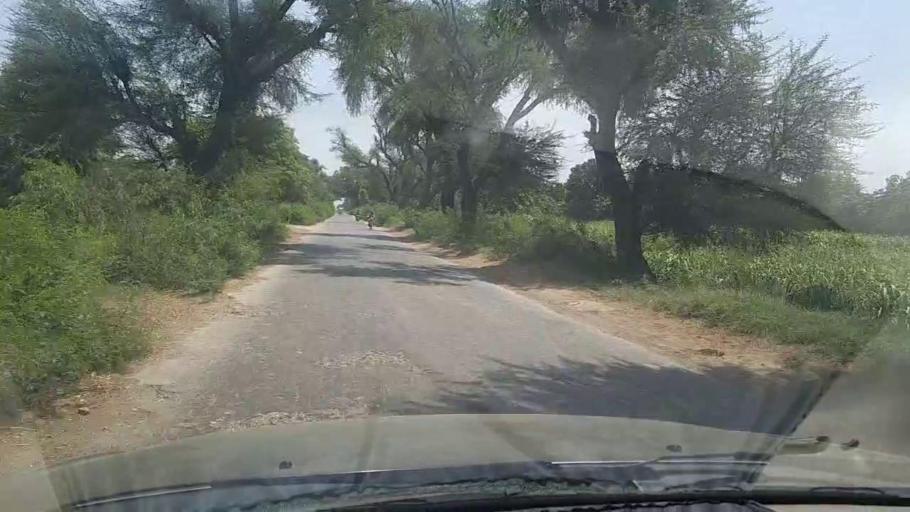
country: PK
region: Sindh
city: Tando Jam
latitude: 25.2792
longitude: 68.6122
